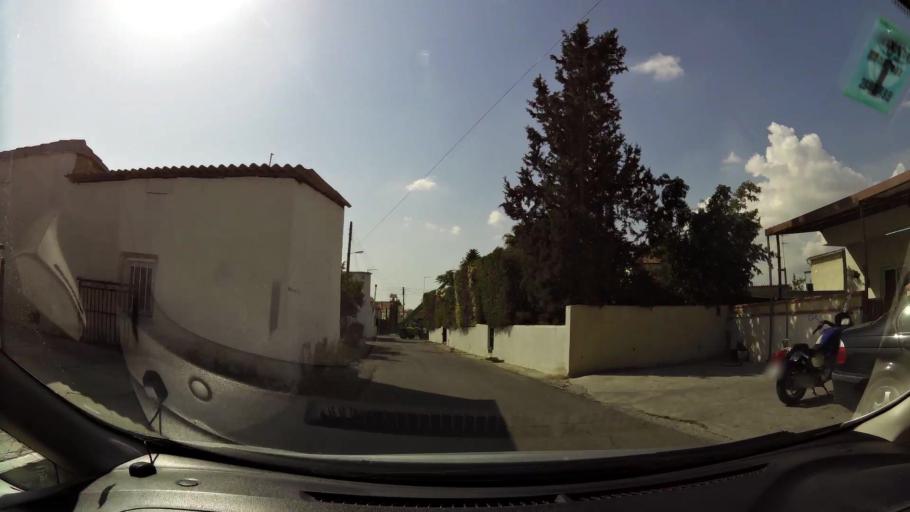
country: CY
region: Larnaka
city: Aradippou
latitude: 34.9534
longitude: 33.5940
